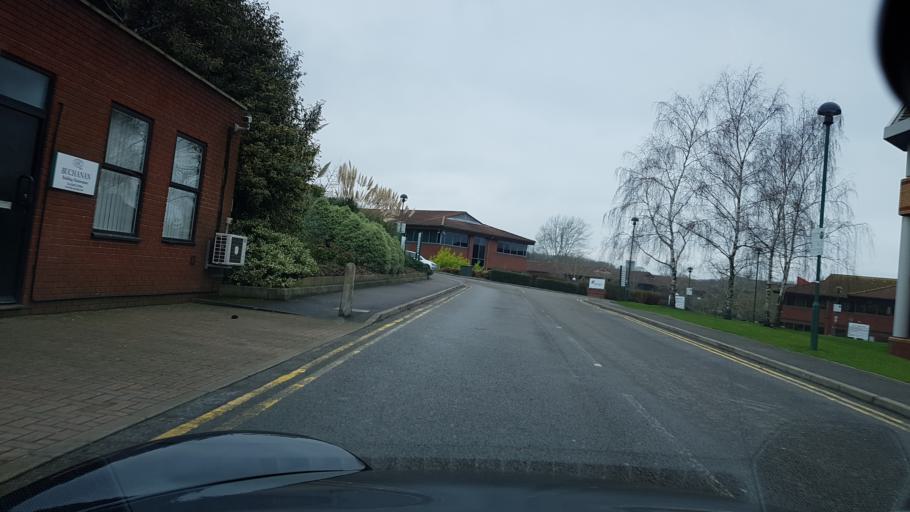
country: GB
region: England
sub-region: Surrey
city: Guildford
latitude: 51.2415
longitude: -0.6119
